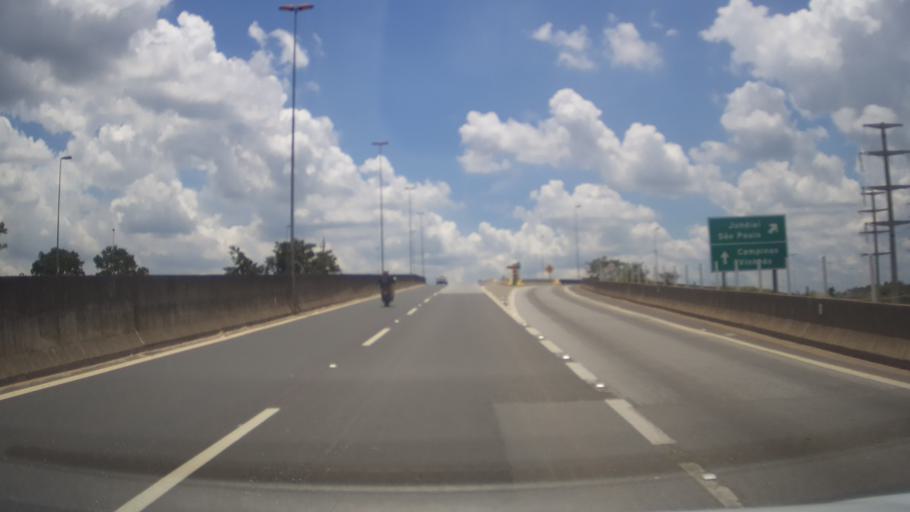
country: BR
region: Sao Paulo
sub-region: Vinhedo
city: Vinhedo
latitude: -23.0616
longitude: -46.9966
